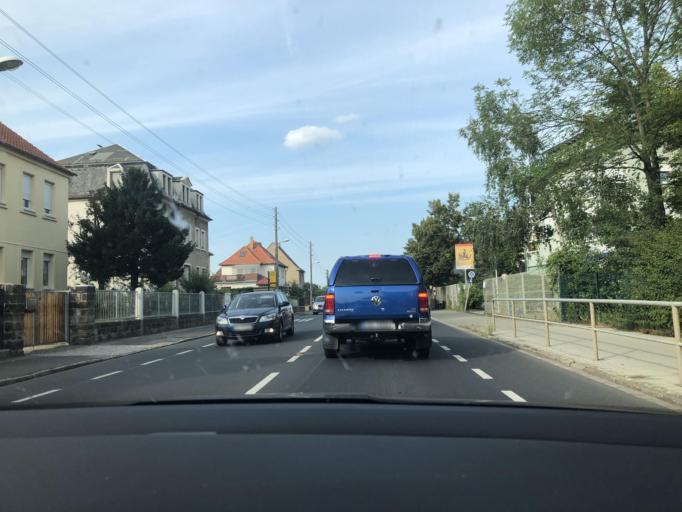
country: DE
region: Saxony
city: Albertstadt
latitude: 51.1169
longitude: 13.7297
